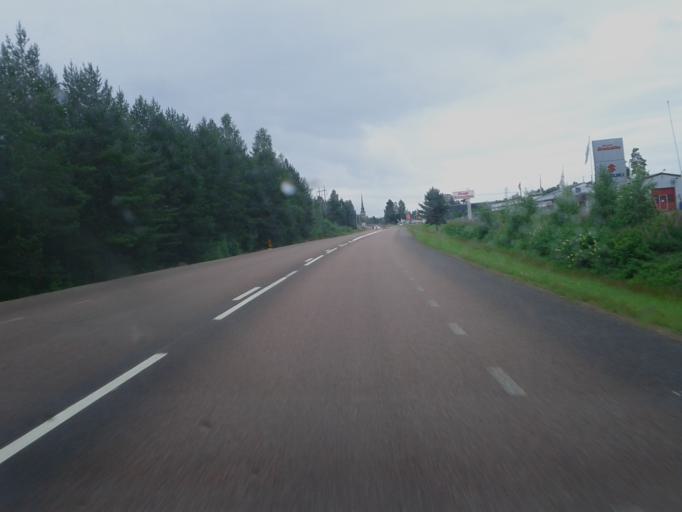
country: SE
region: Dalarna
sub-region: Mora Kommun
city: Mora
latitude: 61.0190
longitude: 14.5382
